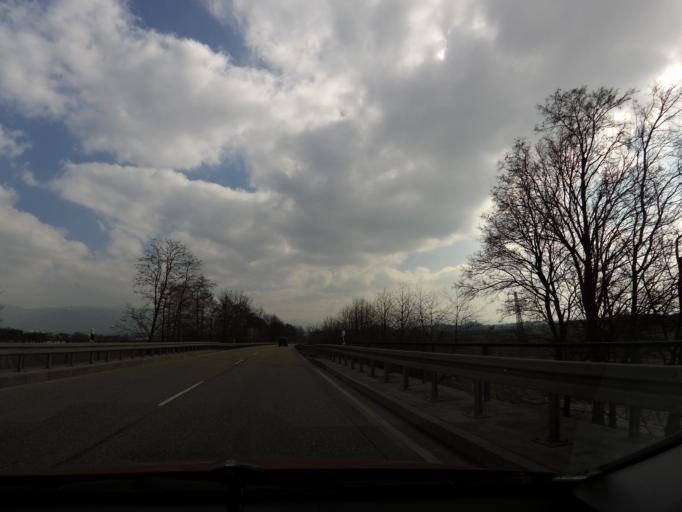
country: DE
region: Baden-Wuerttemberg
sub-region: Freiburg Region
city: Achern
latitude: 48.6376
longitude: 8.0447
